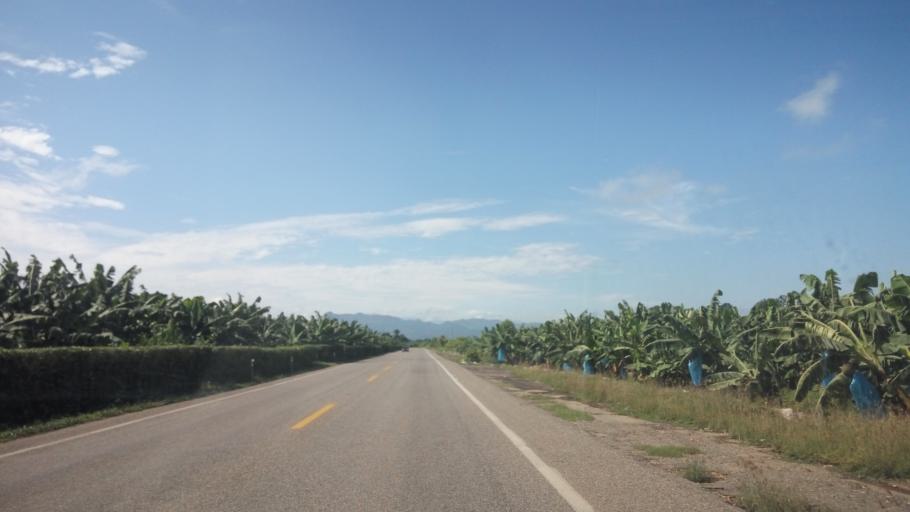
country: MX
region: Tabasco
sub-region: Teapa
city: Eureka y Belen
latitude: 17.6425
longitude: -92.9665
